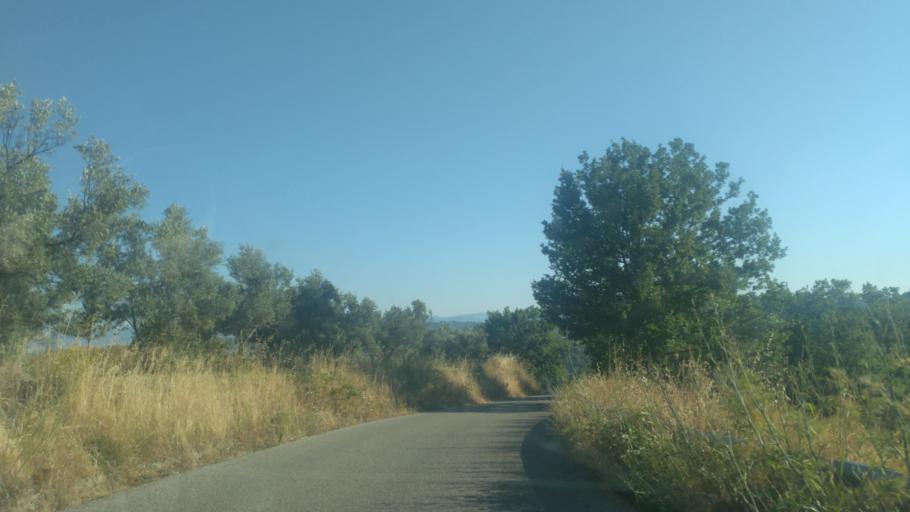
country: IT
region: Calabria
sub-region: Provincia di Catanzaro
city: Squillace
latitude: 38.7690
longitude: 16.5106
